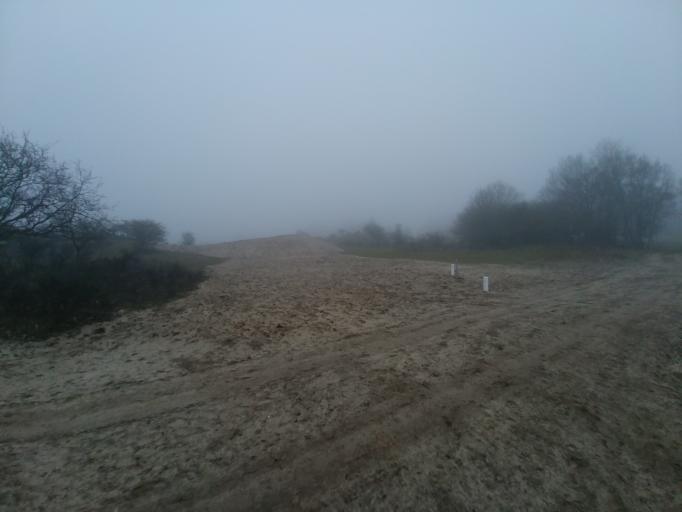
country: NL
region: North Holland
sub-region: Gemeente Zandvoort
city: Zandvoort
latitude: 52.3395
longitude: 4.5514
